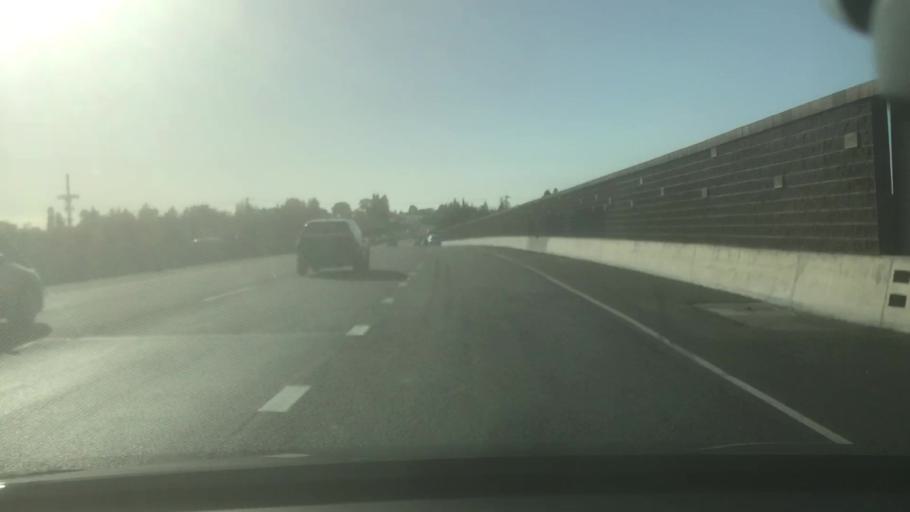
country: US
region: California
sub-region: Alameda County
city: Ashland
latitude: 37.6893
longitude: -122.1165
